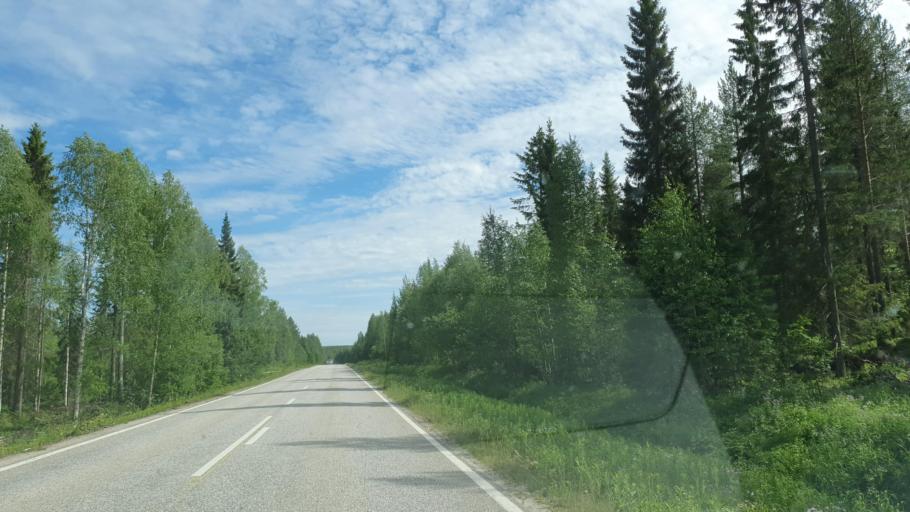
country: FI
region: Kainuu
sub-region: Kehys-Kainuu
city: Hyrynsalmi
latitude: 64.6443
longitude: 28.5575
